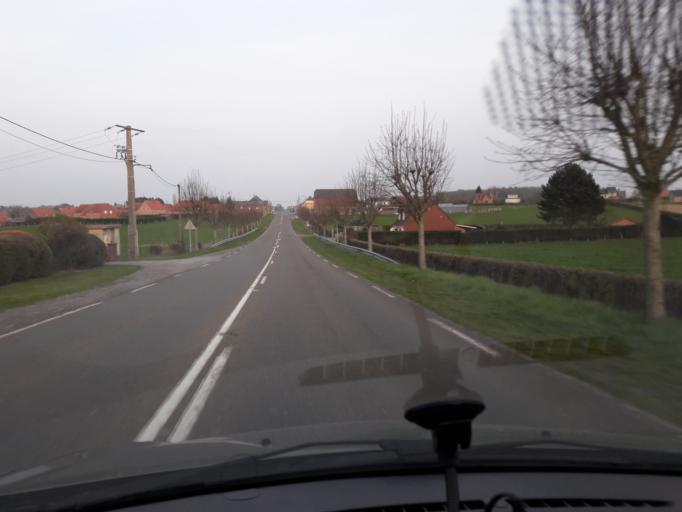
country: FR
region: Nord-Pas-de-Calais
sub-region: Departement du Nord
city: Marpent
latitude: 50.2547
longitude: 4.0694
